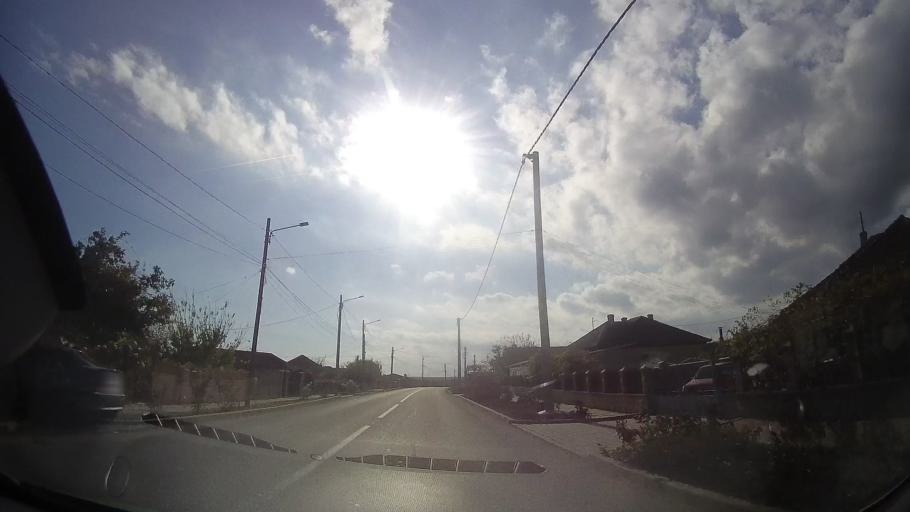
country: RO
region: Constanta
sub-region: Comuna Douazeci si Trei August
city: Dulcesti
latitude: 43.9095
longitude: 28.5495
